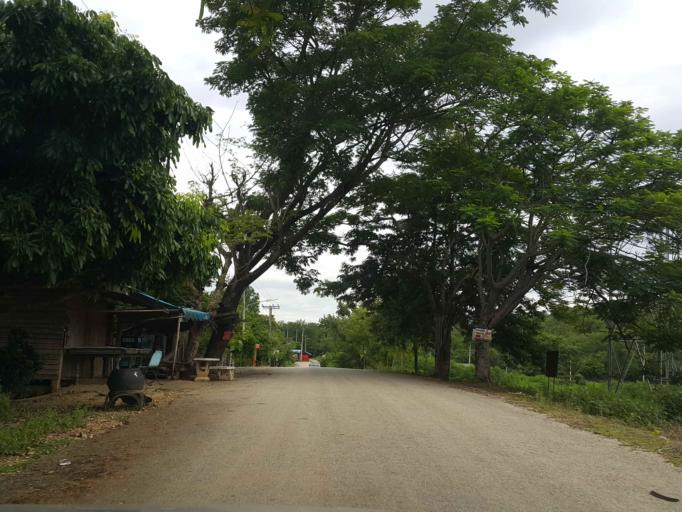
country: TH
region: Sukhothai
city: Thung Saliam
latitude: 17.3456
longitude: 99.4380
